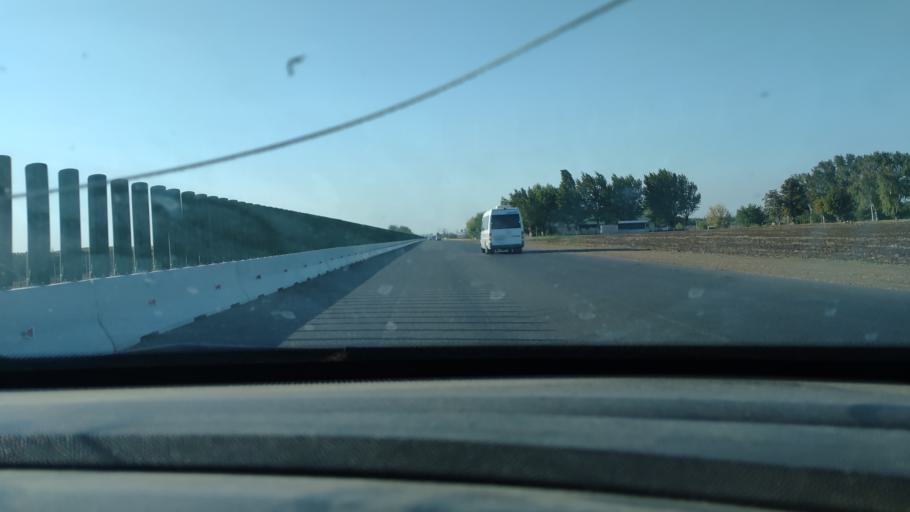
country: RU
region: Krasnodarskiy
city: Medvedovskaya
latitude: 45.4752
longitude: 38.9733
